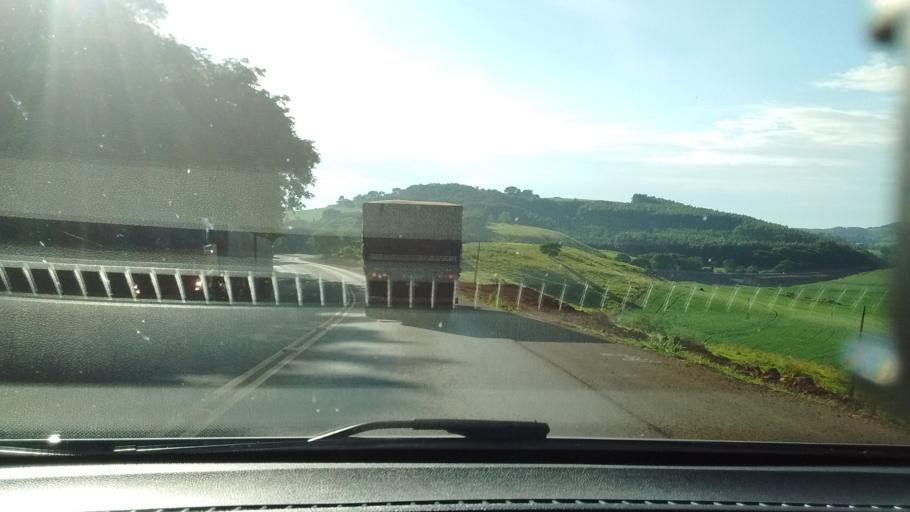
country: BR
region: Parana
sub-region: Cascavel
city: Cascavel
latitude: -25.2009
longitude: -53.6013
